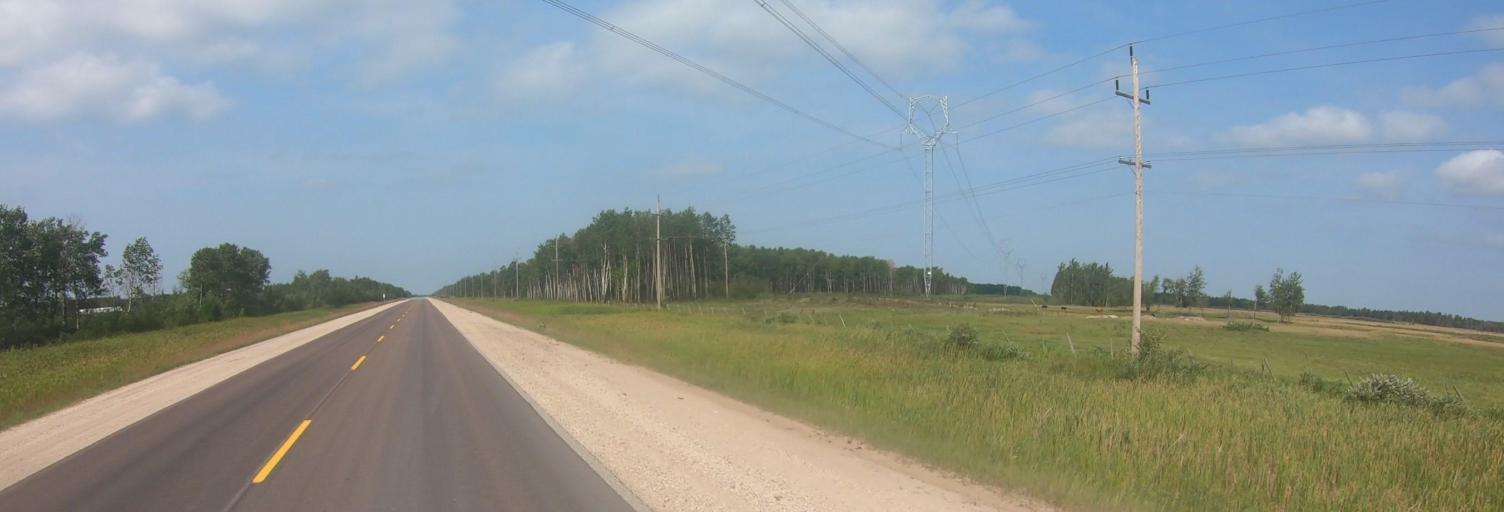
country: CA
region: Manitoba
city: La Broquerie
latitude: 49.2670
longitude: -96.4203
